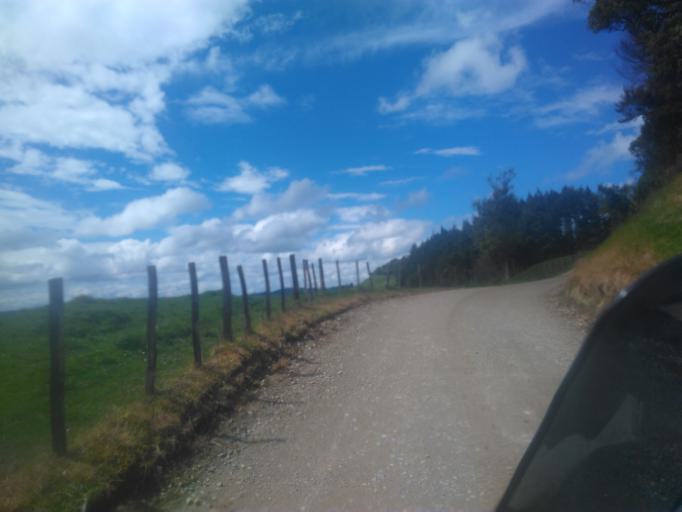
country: NZ
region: Hawke's Bay
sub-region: Wairoa District
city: Wairoa
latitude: -38.7752
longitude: 177.6346
